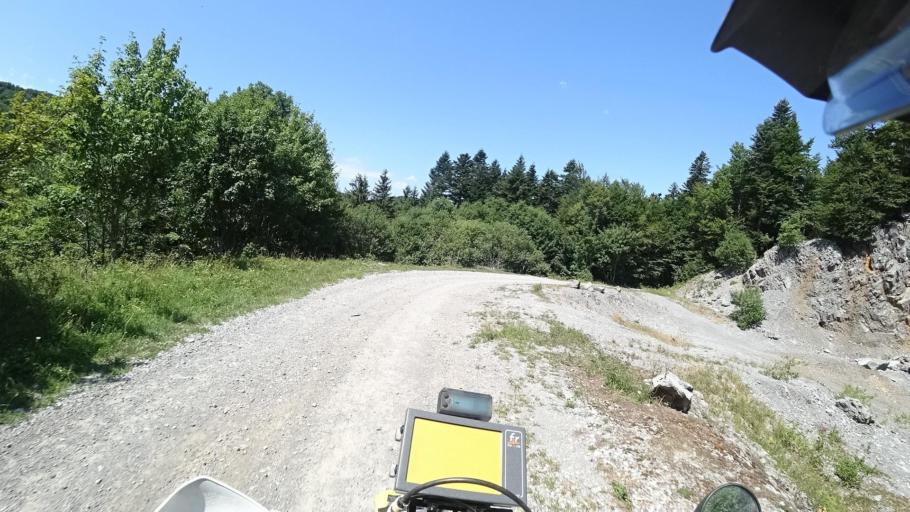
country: HR
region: Primorsko-Goranska
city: Vrbovsko
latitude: 45.2688
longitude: 14.9464
